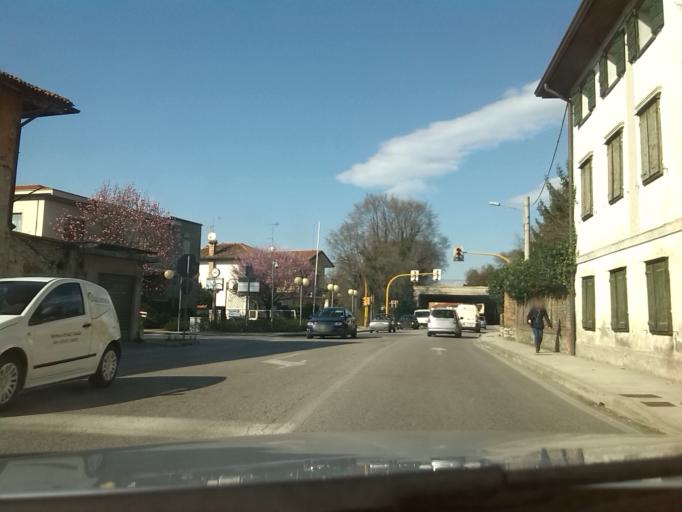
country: IT
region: Friuli Venezia Giulia
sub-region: Provincia di Gorizia
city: Fogliano
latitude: 45.8662
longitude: 13.4815
